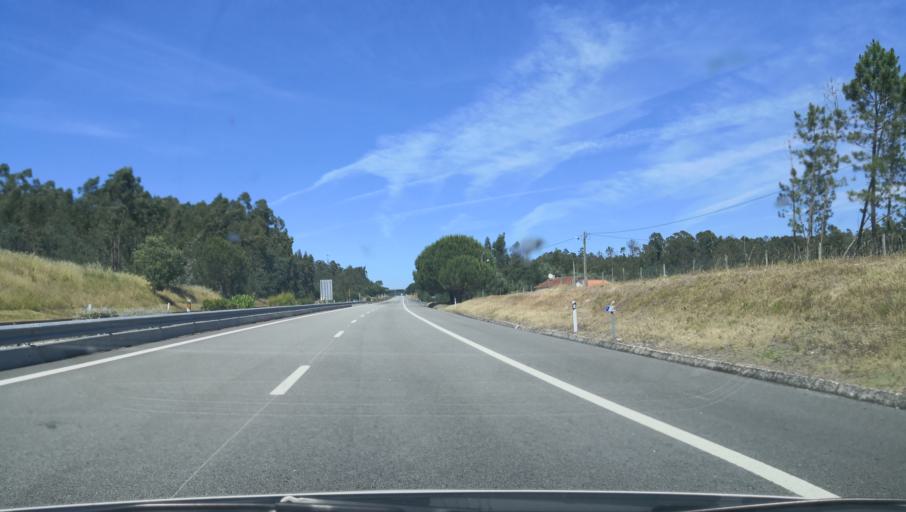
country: PT
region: Coimbra
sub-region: Montemor-O-Velho
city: Montemor-o-Velho
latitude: 40.2232
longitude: -8.6734
